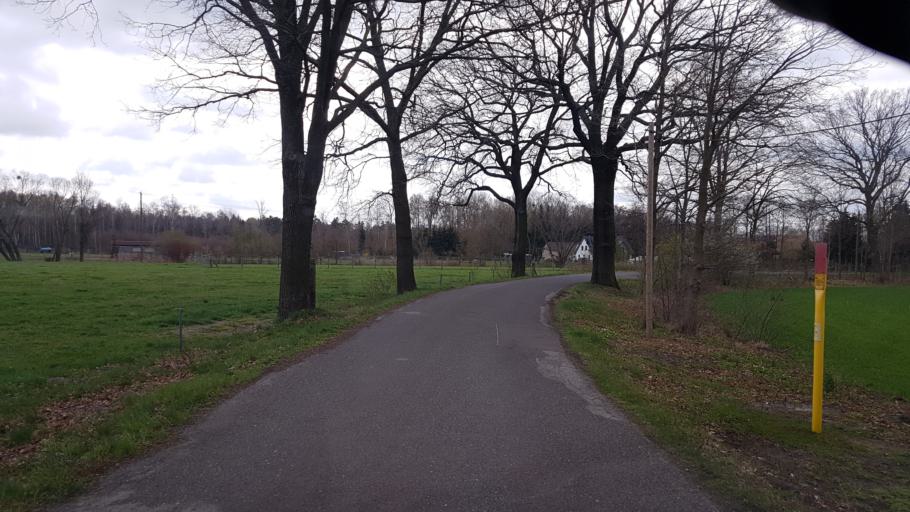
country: DE
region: Brandenburg
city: Lauchhammer
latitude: 51.4593
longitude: 13.7725
